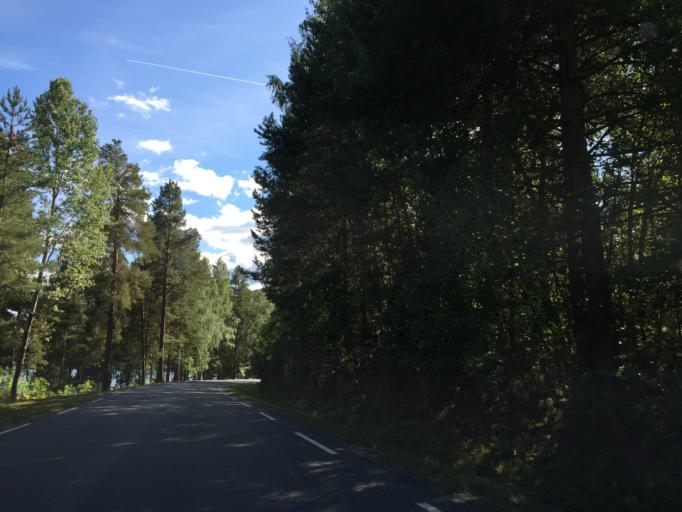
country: NO
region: Buskerud
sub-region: Ovre Eiker
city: Hokksund
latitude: 59.6989
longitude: 9.8440
